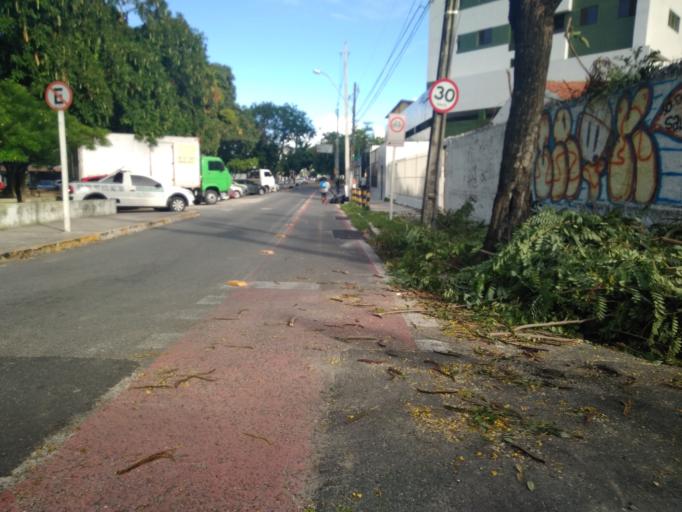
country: BR
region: Pernambuco
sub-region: Recife
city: Recife
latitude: -8.0354
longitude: -34.8932
